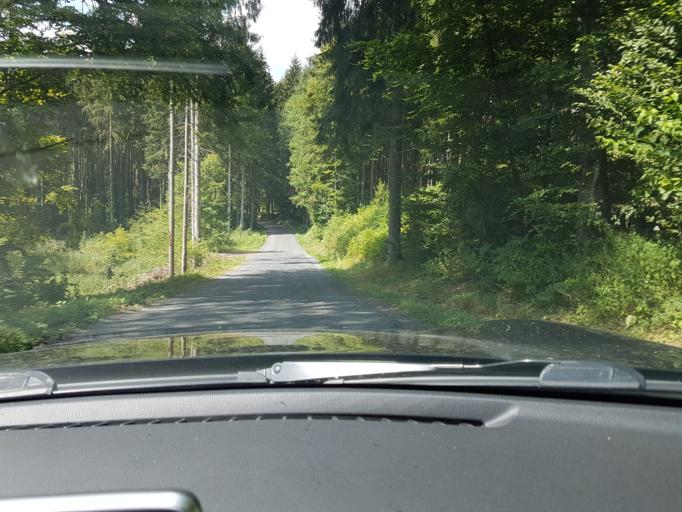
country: DE
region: Baden-Wuerttemberg
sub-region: Karlsruhe Region
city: Fahrenbach
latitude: 49.4186
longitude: 9.1848
